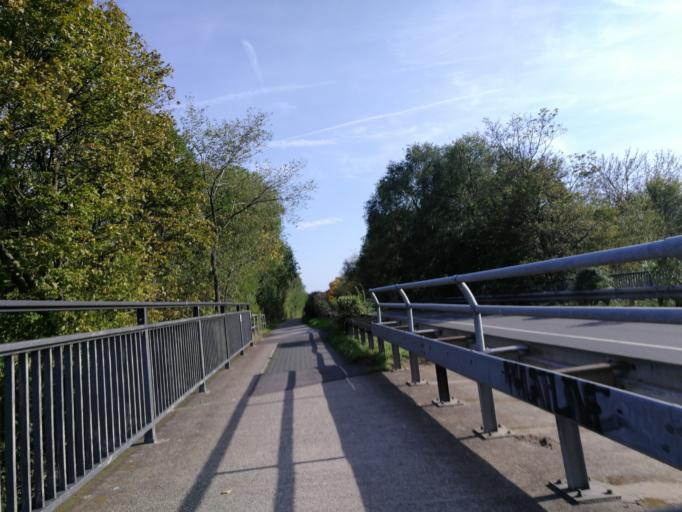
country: DE
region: North Rhine-Westphalia
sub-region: Regierungsbezirk Dusseldorf
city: Dusseldorf
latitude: 51.1713
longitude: 6.7755
